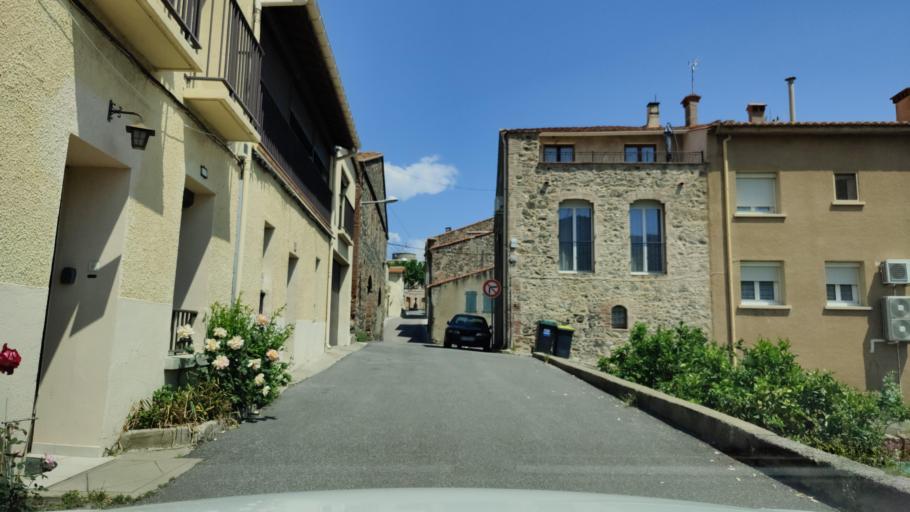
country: FR
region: Languedoc-Roussillon
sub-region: Departement des Pyrenees-Orientales
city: Baixas
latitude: 42.7785
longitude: 2.7856
